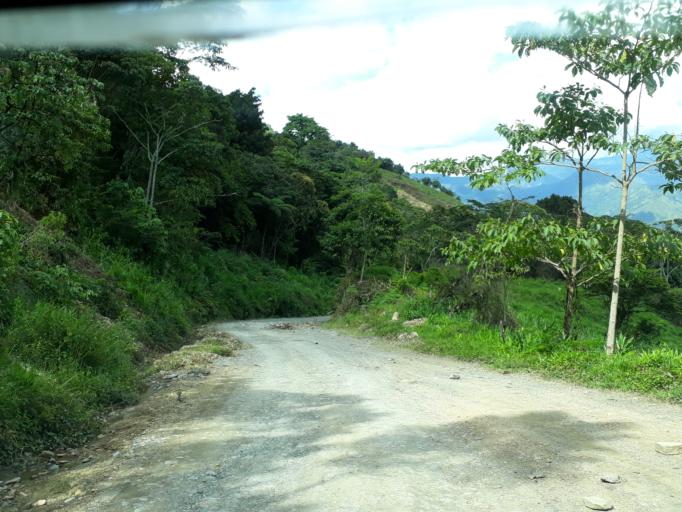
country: CO
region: Cundinamarca
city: Topaipi
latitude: 5.3883
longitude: -74.1972
